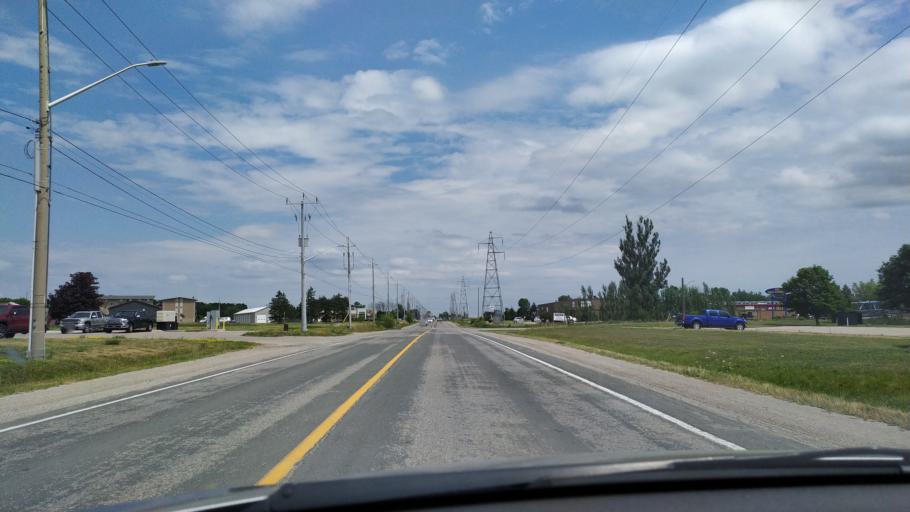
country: CA
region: Ontario
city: Stratford
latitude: 43.3530
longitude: -80.9792
